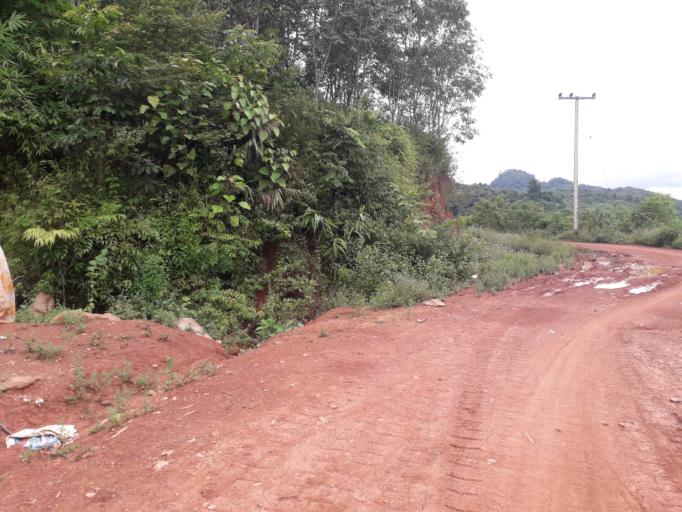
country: CN
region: Yunnan
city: Menglie
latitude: 22.2006
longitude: 101.6740
